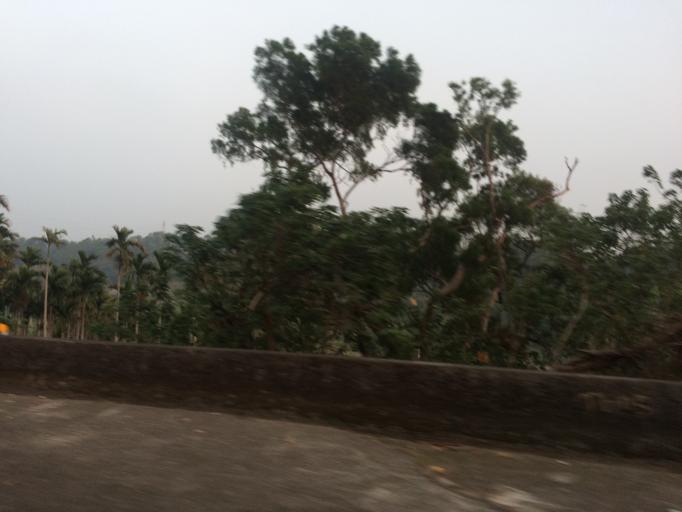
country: TW
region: Taiwan
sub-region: Hsinchu
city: Hsinchu
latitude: 24.7045
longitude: 120.9255
